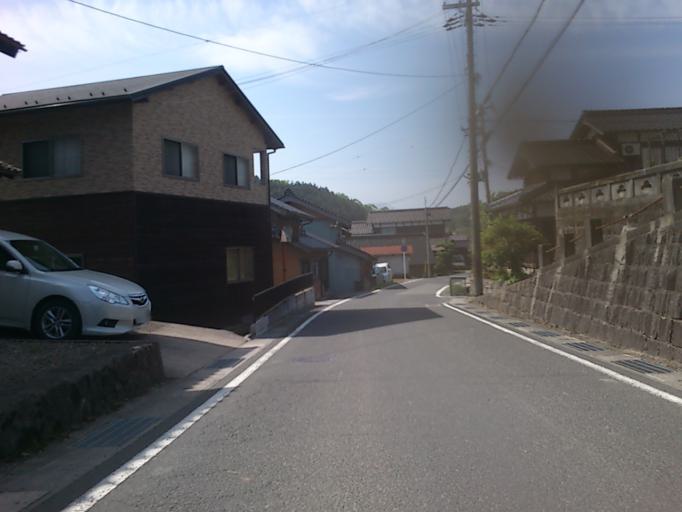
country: JP
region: Kyoto
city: Miyazu
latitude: 35.5628
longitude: 135.1130
